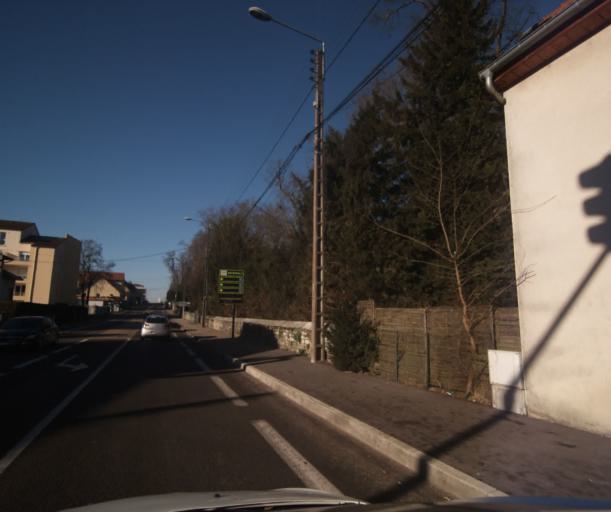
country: FR
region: Franche-Comte
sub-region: Departement du Doubs
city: Beure
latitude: 47.2294
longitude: 5.9902
